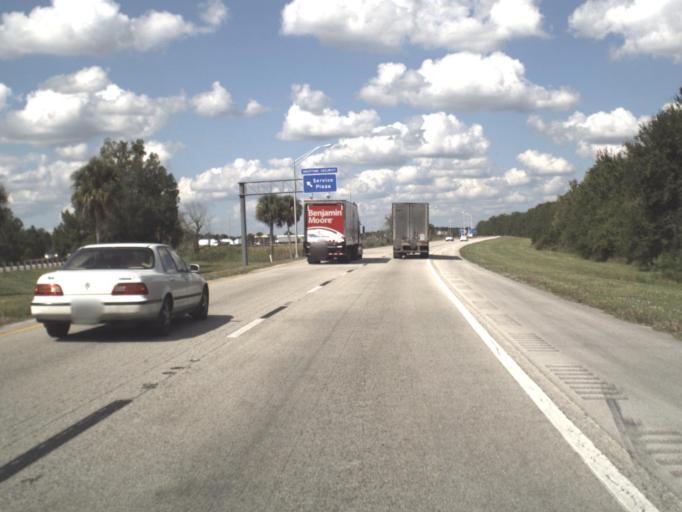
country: US
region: Florida
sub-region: Indian River County
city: Fellsmere
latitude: 27.5954
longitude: -80.8180
